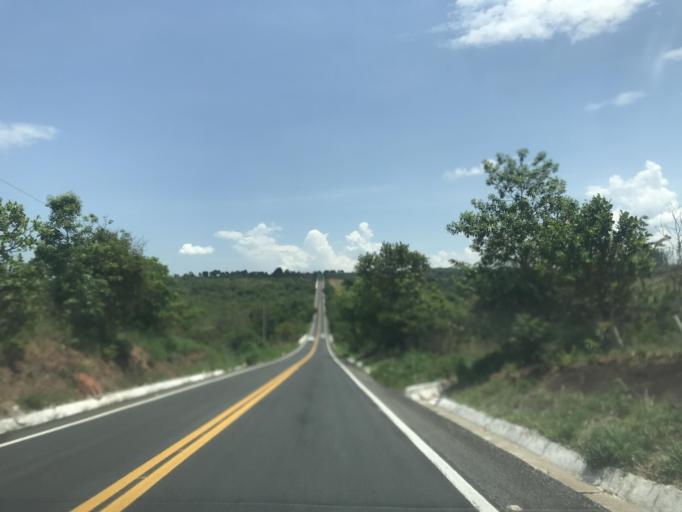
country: BR
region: Goias
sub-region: Bela Vista De Goias
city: Bela Vista de Goias
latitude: -17.1206
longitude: -48.6675
